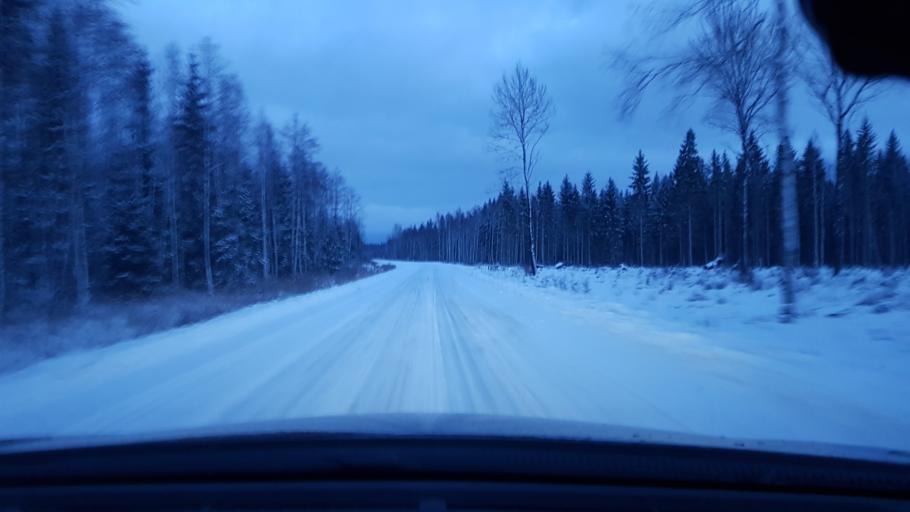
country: EE
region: Harju
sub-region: Nissi vald
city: Turba
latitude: 59.1275
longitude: 24.0811
